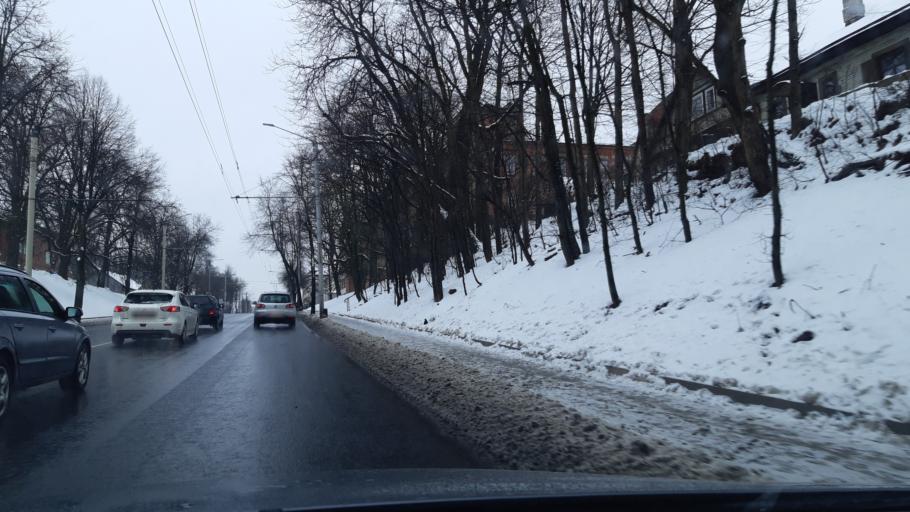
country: LT
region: Kauno apskritis
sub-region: Kaunas
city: Kaunas
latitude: 54.9019
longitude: 23.9103
